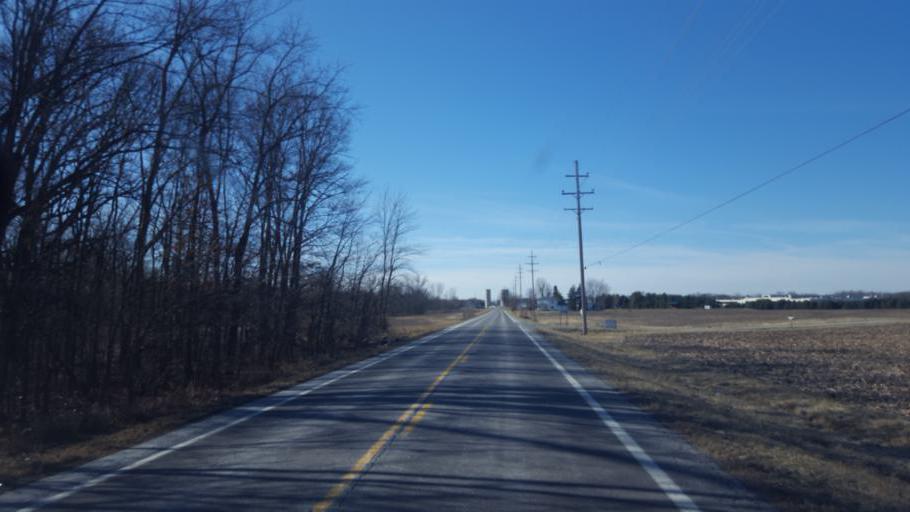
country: US
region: Ohio
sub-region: Marion County
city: Marion
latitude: 40.5430
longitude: -83.2006
